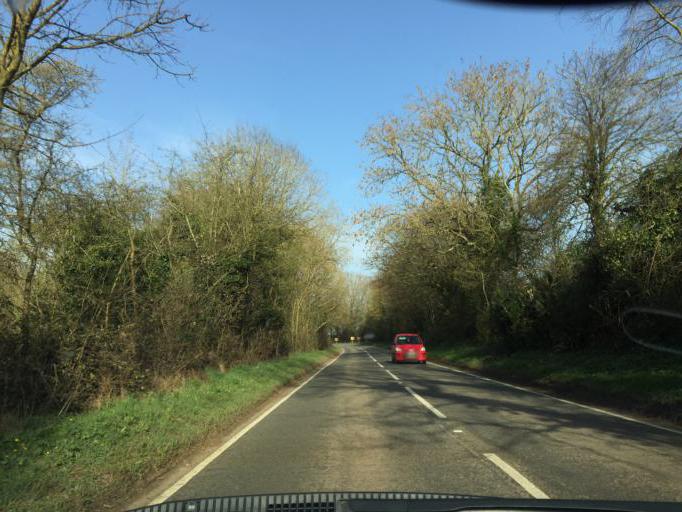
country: GB
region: England
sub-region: Oxfordshire
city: Bloxham
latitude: 52.0503
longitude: -1.3736
